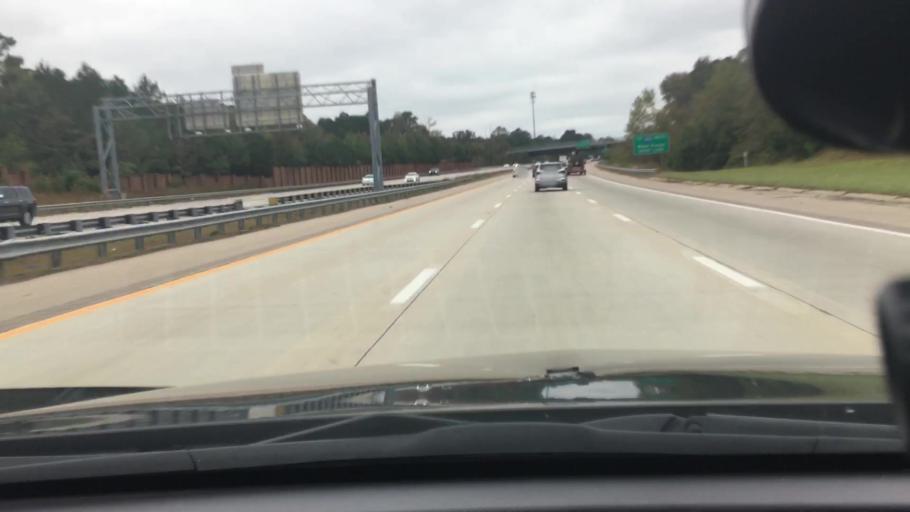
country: US
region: North Carolina
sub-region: Wake County
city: Knightdale
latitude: 35.7734
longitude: -78.5436
